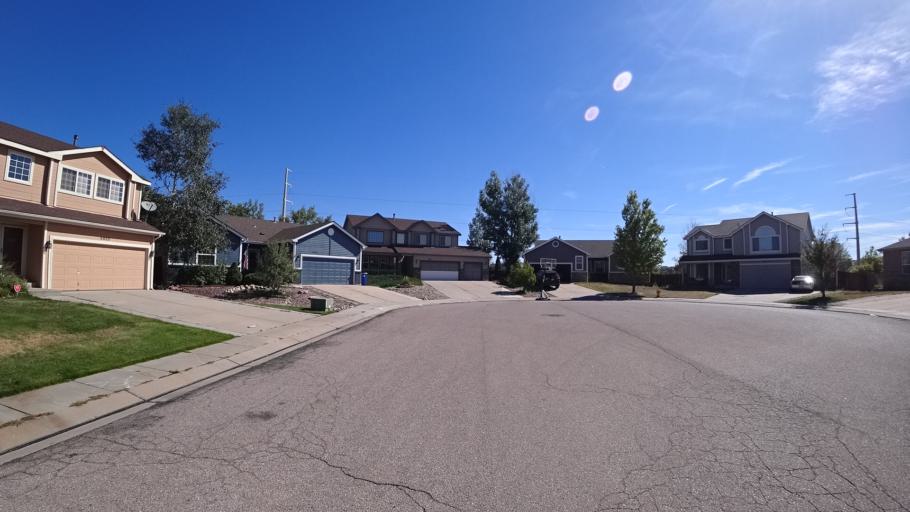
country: US
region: Colorado
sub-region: El Paso County
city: Black Forest
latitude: 38.9499
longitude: -104.7225
